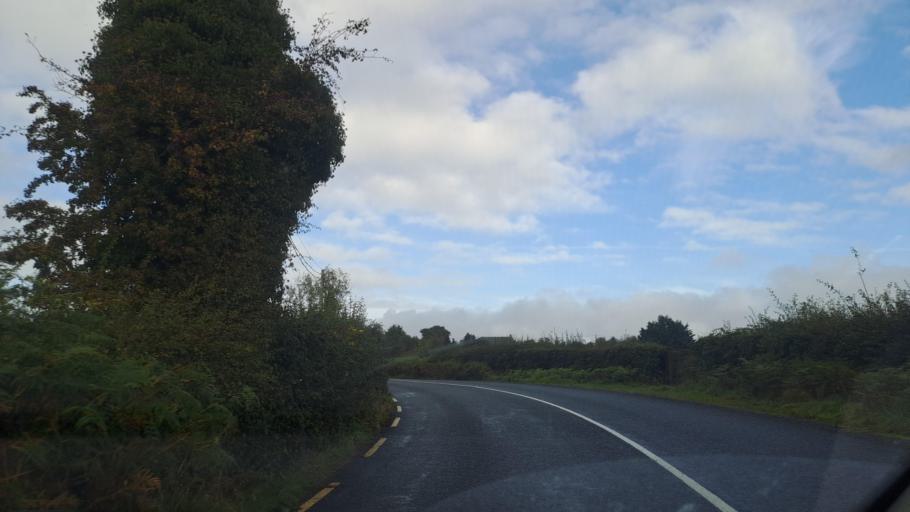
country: IE
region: Ulster
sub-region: County Monaghan
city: Carrickmacross
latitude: 53.9304
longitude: -6.7156
